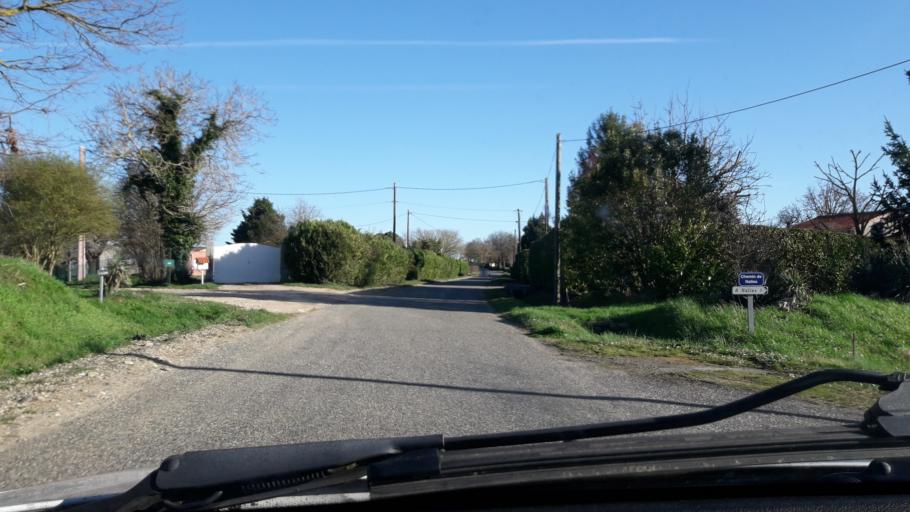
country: FR
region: Midi-Pyrenees
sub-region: Departement du Gers
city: Samatan
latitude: 43.5938
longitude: 0.9906
